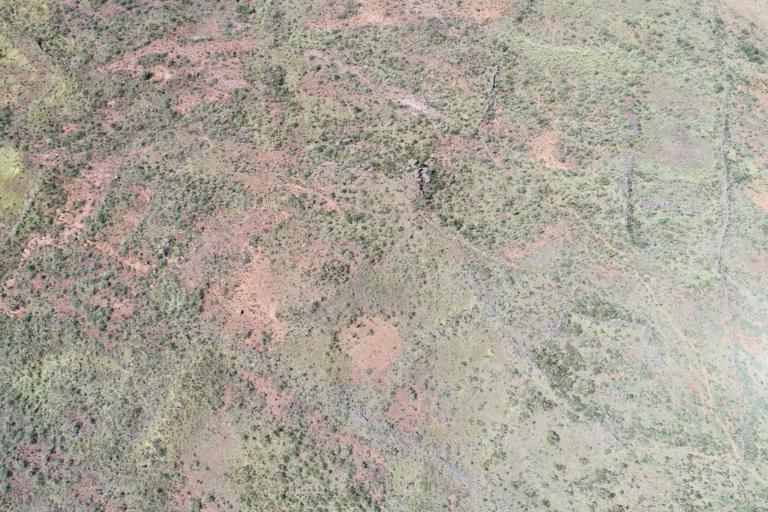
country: BO
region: La Paz
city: Tiahuanaco
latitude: -16.6056
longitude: -68.7741
